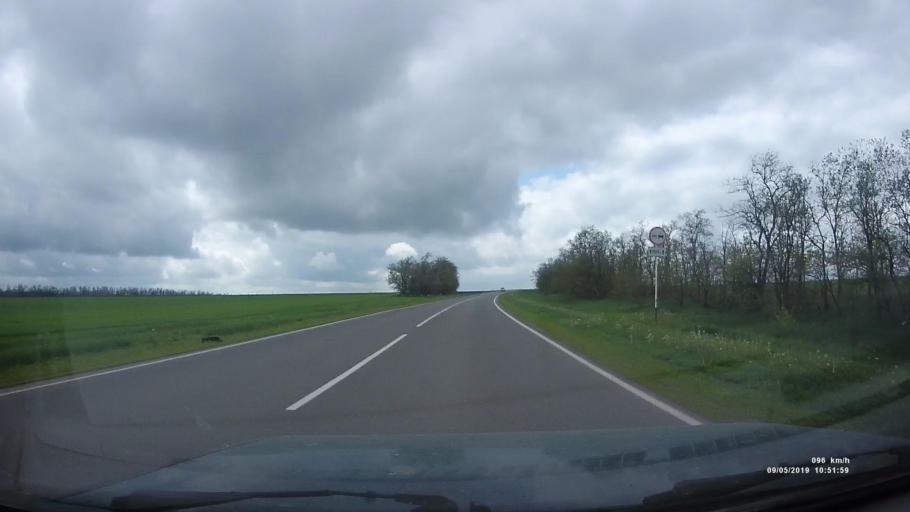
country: RU
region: Rostov
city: Peshkovo
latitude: 46.9074
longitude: 39.3549
